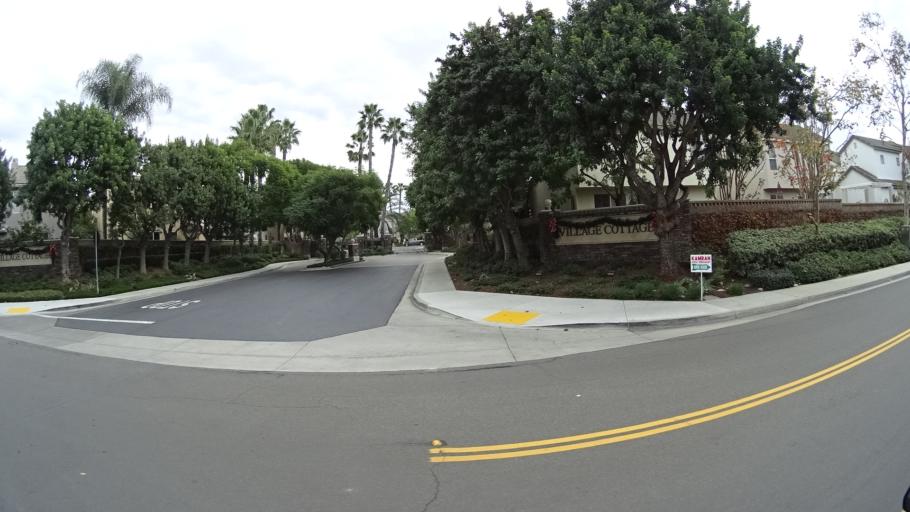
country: US
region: California
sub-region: Orange County
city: Aliso Viejo
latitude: 33.5644
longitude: -117.7333
